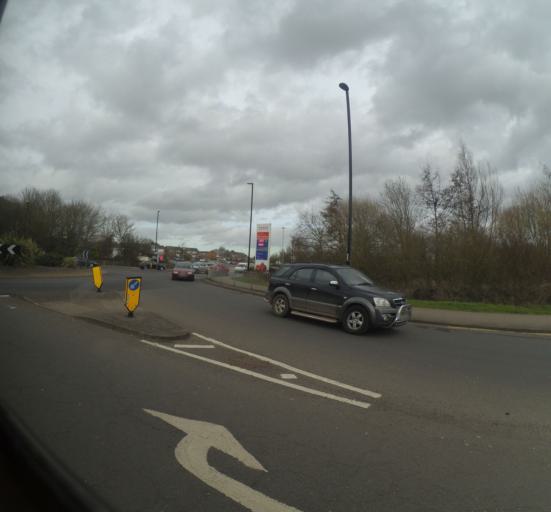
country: GB
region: England
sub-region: Warwickshire
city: Ryton on Dunsmore
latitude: 52.4127
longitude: -1.4438
